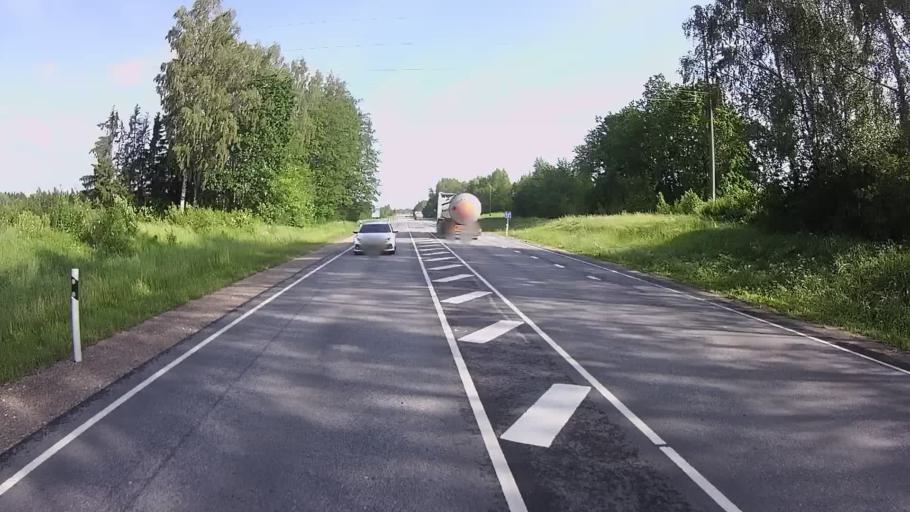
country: EE
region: Viljandimaa
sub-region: Viljandi linn
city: Viljandi
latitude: 58.3443
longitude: 25.5657
